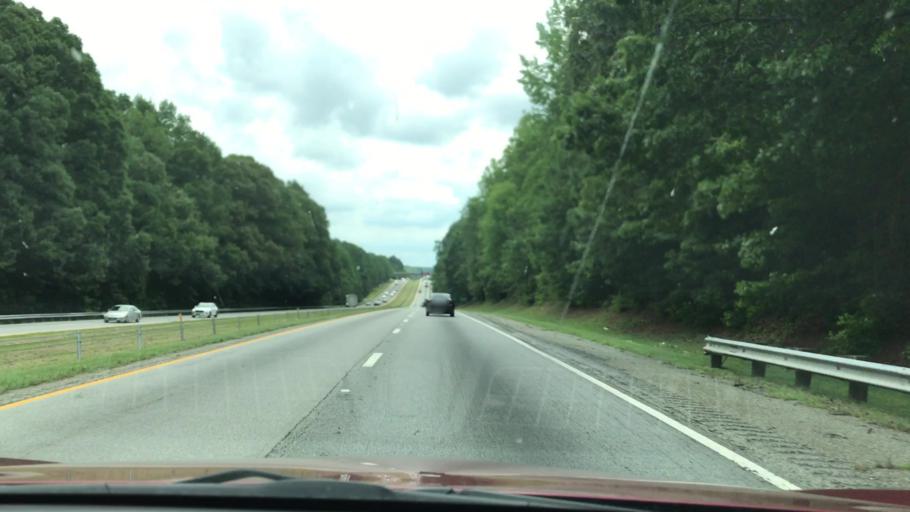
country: US
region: South Carolina
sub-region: Lexington County
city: Chapin
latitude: 34.1964
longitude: -81.3567
